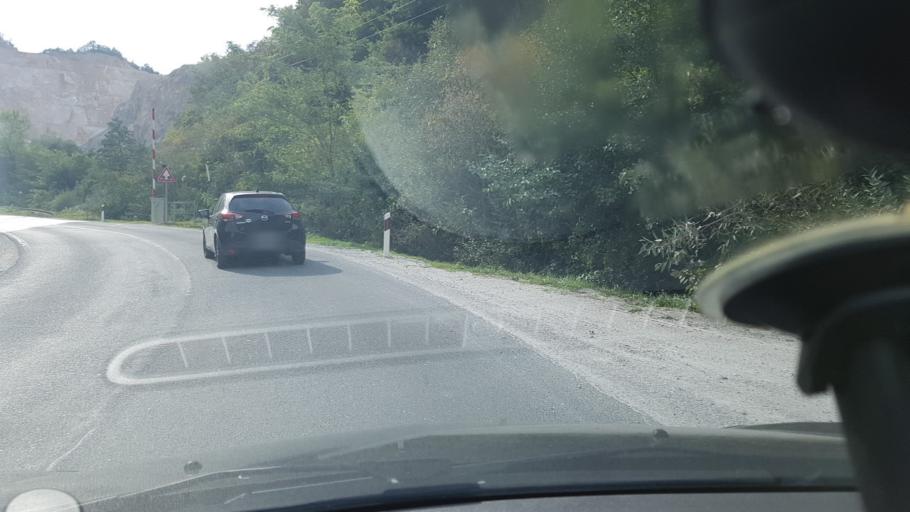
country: HR
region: Varazdinska
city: Lepoglava
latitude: 46.1935
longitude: 15.9908
